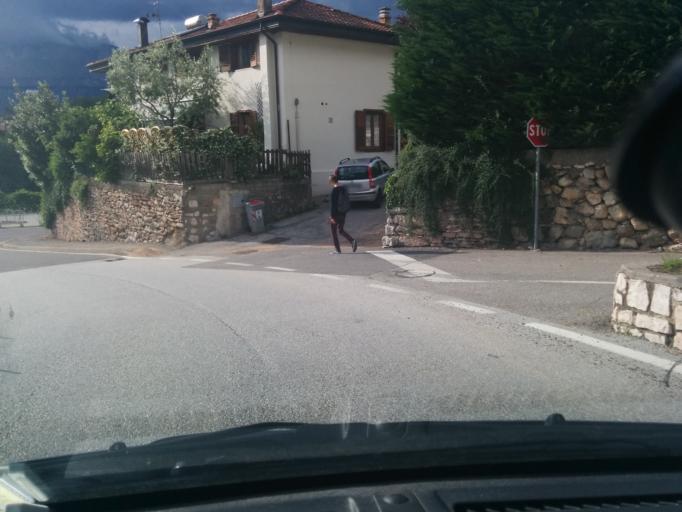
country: IT
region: Trentino-Alto Adige
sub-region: Provincia di Trento
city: Povo
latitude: 46.0728
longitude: 11.1531
